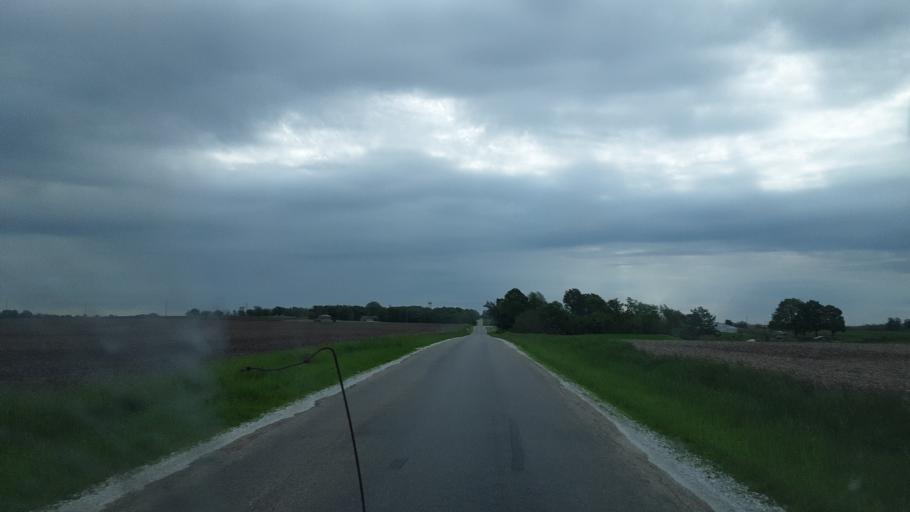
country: US
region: Illinois
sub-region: Fulton County
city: Astoria
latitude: 40.3643
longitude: -90.4467
